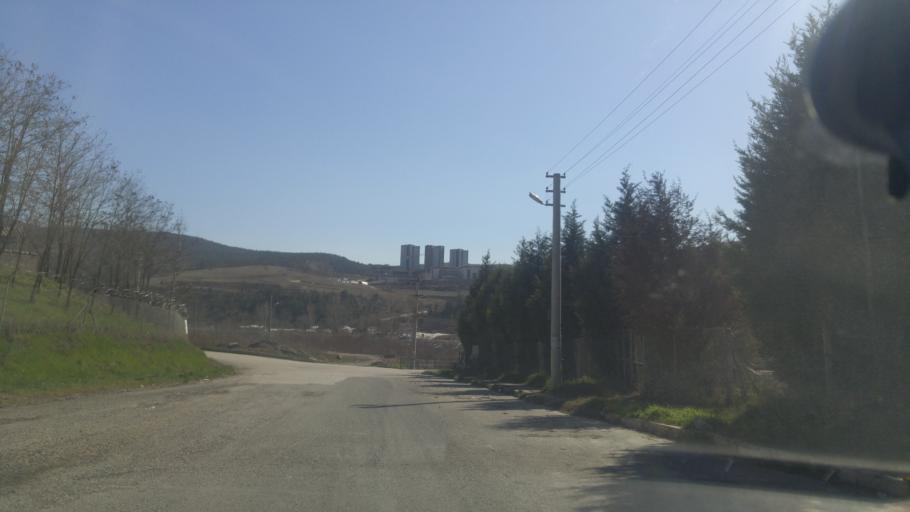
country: TR
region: Karabuk
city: Karabuk
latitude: 41.2148
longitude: 32.6582
